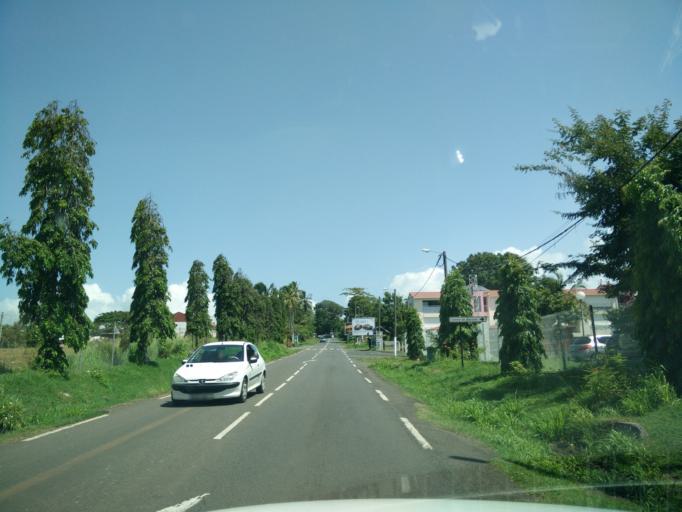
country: GP
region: Guadeloupe
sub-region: Guadeloupe
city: Petit-Bourg
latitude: 16.1819
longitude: -61.5879
